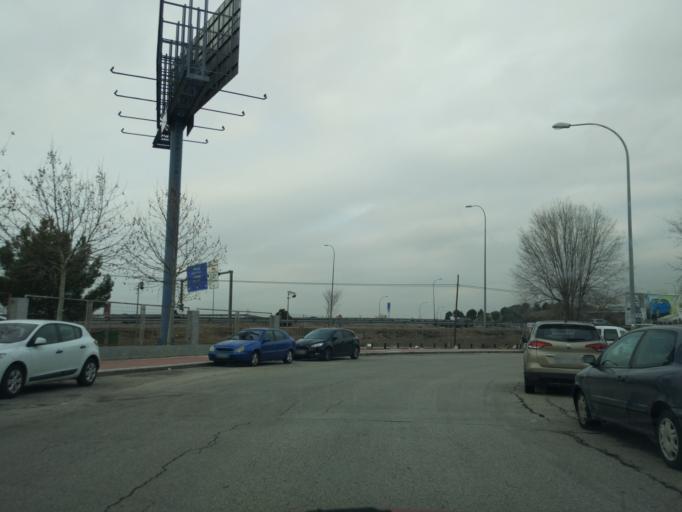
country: ES
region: Madrid
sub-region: Provincia de Madrid
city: Torrejon de Ardoz
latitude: 40.4538
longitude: -3.5079
